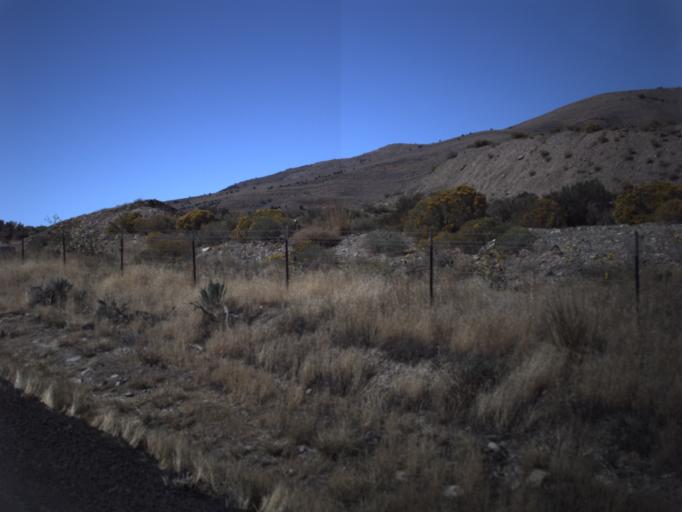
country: US
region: Utah
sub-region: Utah County
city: Saratoga Springs
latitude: 40.2152
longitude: -111.8867
